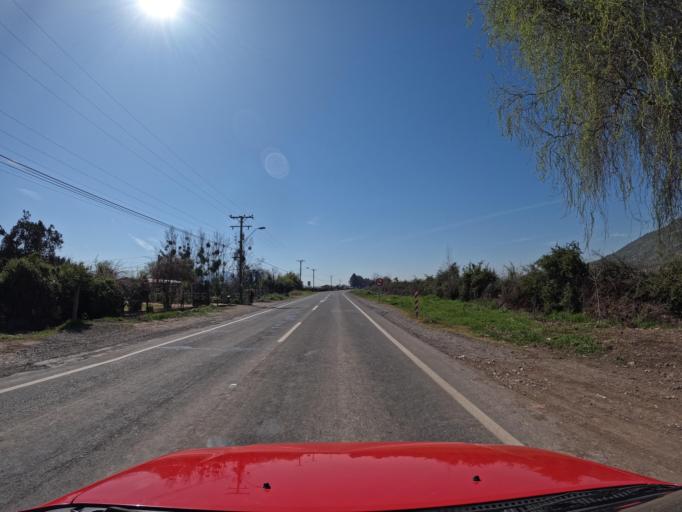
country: CL
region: Maule
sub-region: Provincia de Curico
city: Rauco
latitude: -35.0112
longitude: -71.4161
